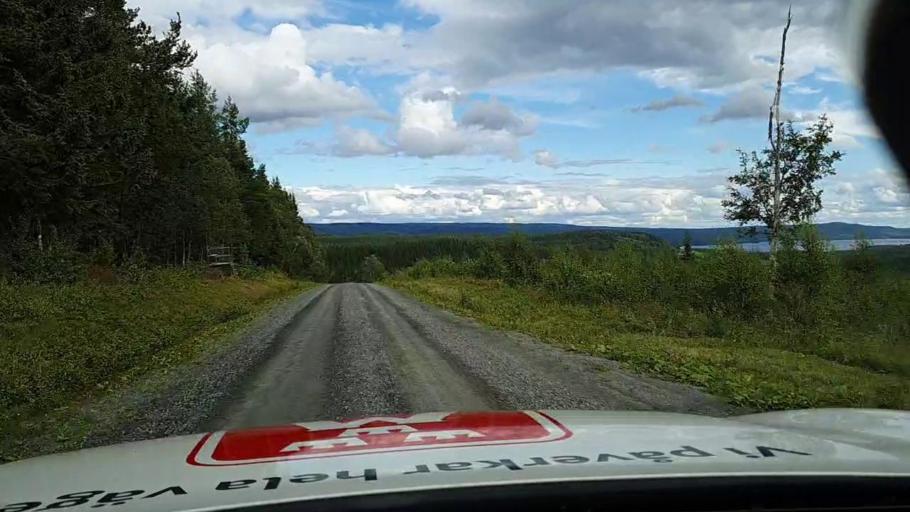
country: SE
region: Jaemtland
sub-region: Krokoms Kommun
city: Valla
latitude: 63.5751
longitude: 13.9377
